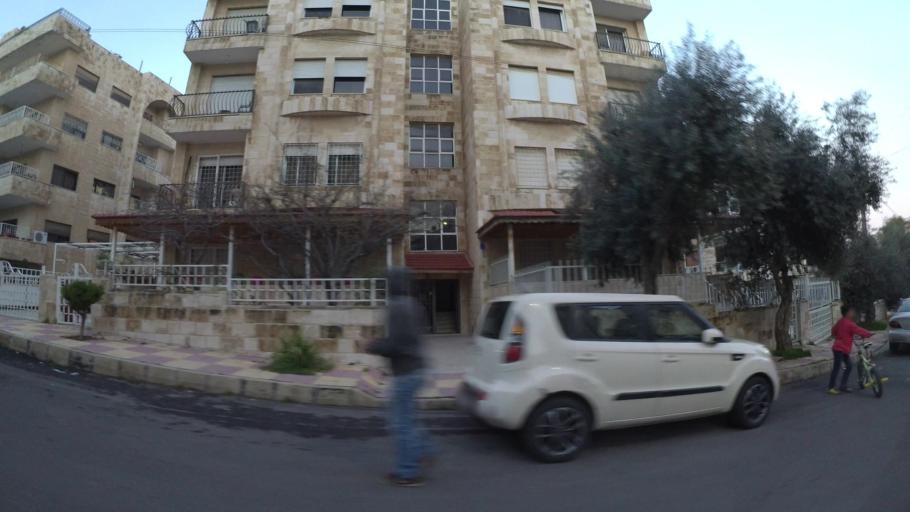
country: JO
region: Amman
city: Al Jubayhah
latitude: 31.9917
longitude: 35.8846
